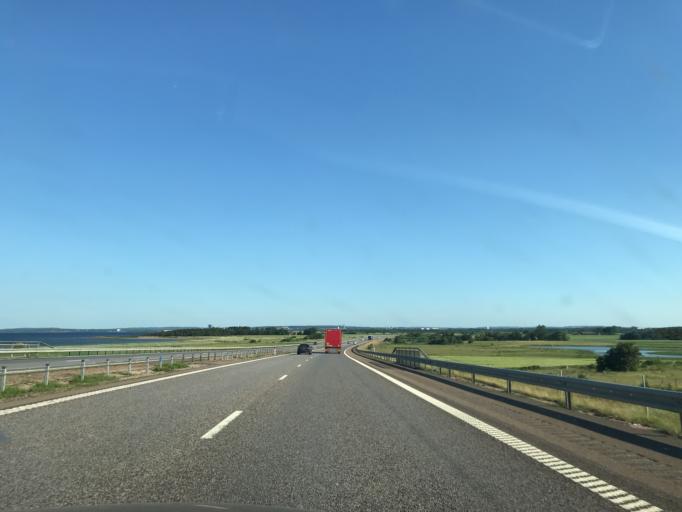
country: SE
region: Halland
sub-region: Halmstads Kommun
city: Paarp
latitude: 56.6064
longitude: 12.9214
